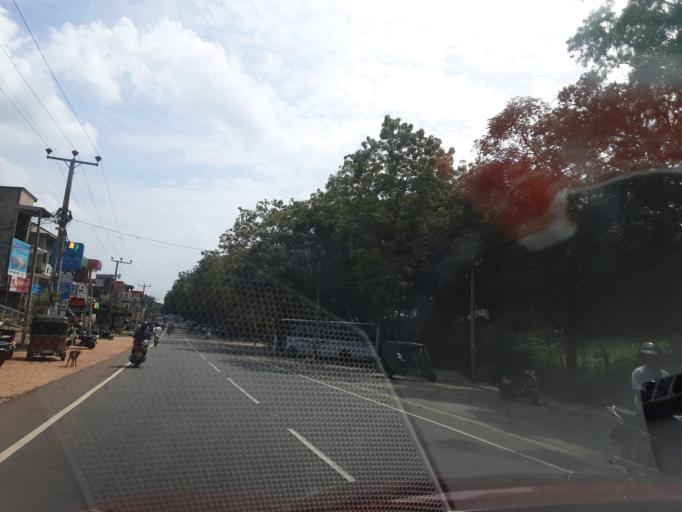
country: LK
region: Northern Province
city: Vavuniya
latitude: 8.5424
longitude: 80.4913
